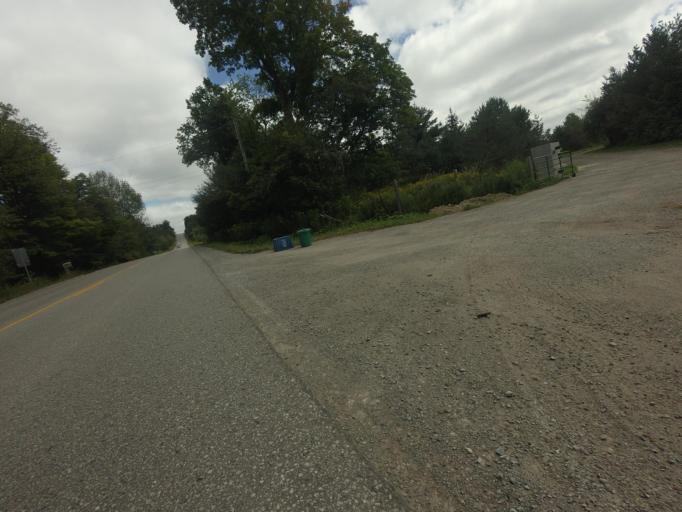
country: CA
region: Ontario
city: Uxbridge
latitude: 44.1252
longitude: -79.1676
